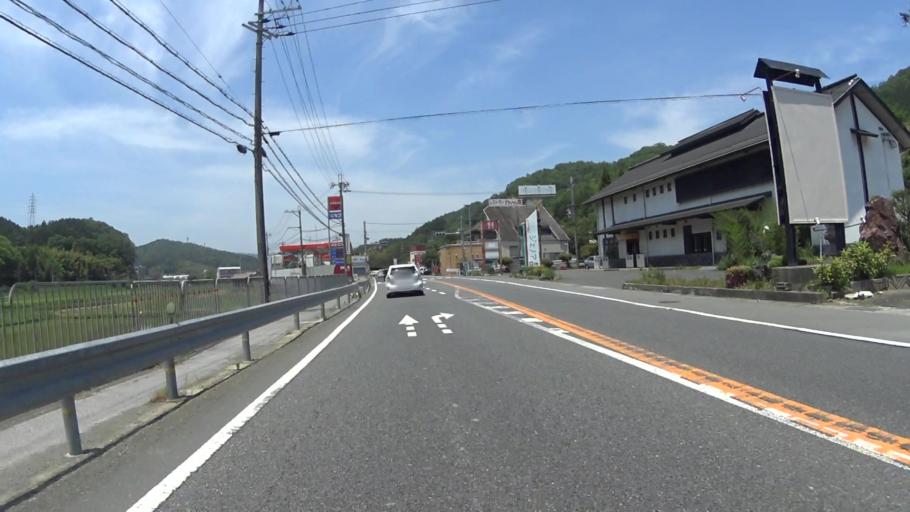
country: JP
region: Kyoto
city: Kameoka
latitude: 35.0982
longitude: 135.4940
